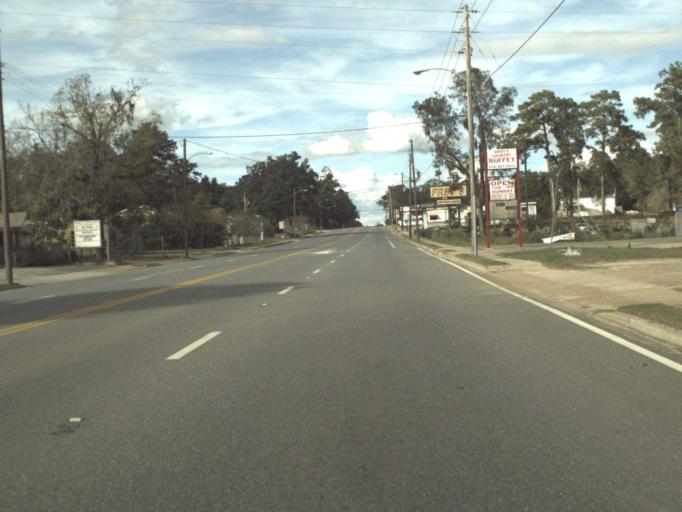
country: US
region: Florida
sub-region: Jefferson County
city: Monticello
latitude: 30.5532
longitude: -83.8701
